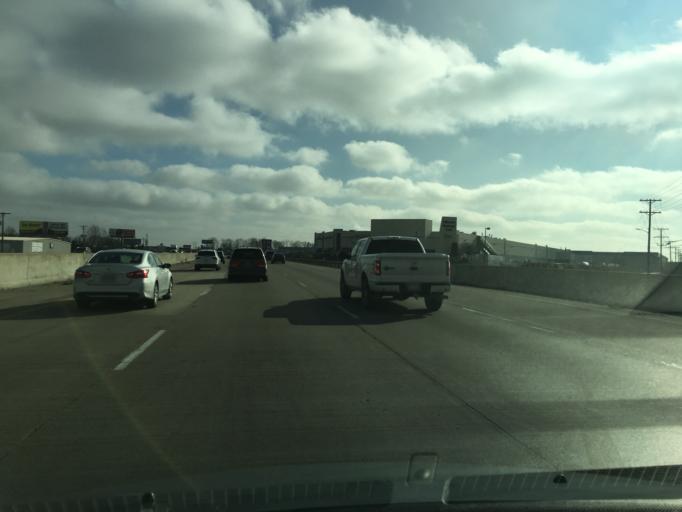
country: US
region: Indiana
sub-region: Boone County
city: Lebanon
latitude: 40.0436
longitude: -86.4867
